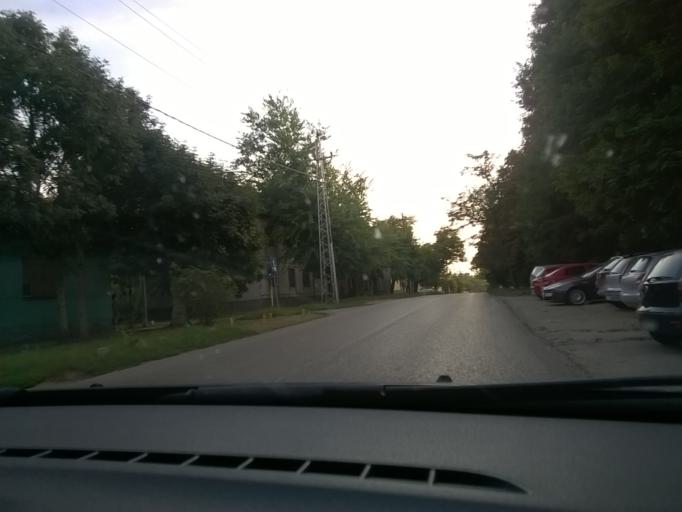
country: RS
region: Autonomna Pokrajina Vojvodina
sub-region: Juznobanatski Okrug
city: Vrsac
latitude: 45.1120
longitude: 21.2946
